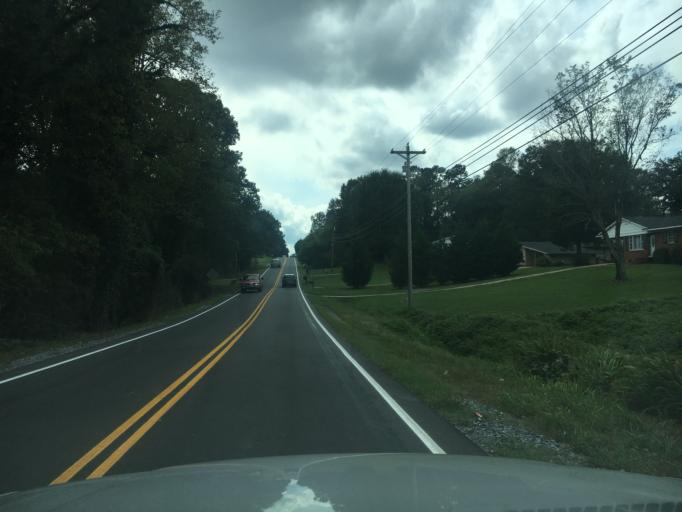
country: US
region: North Carolina
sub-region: Gaston County
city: Bessemer City
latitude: 35.2975
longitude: -81.2302
